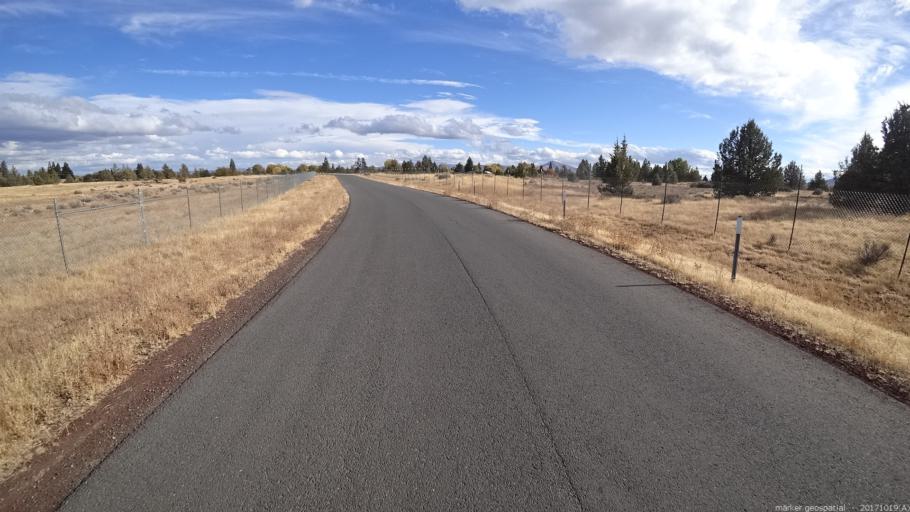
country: US
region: California
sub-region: Shasta County
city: Burney
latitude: 41.0104
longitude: -121.4416
